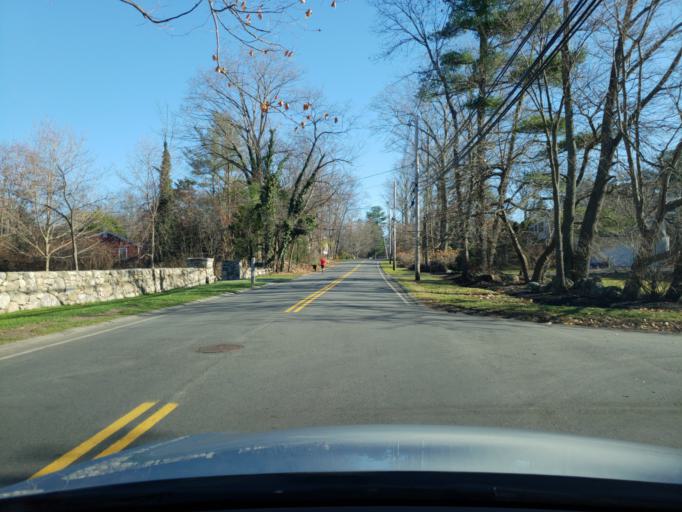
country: US
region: Massachusetts
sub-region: Essex County
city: Andover
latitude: 42.6390
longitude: -71.1369
